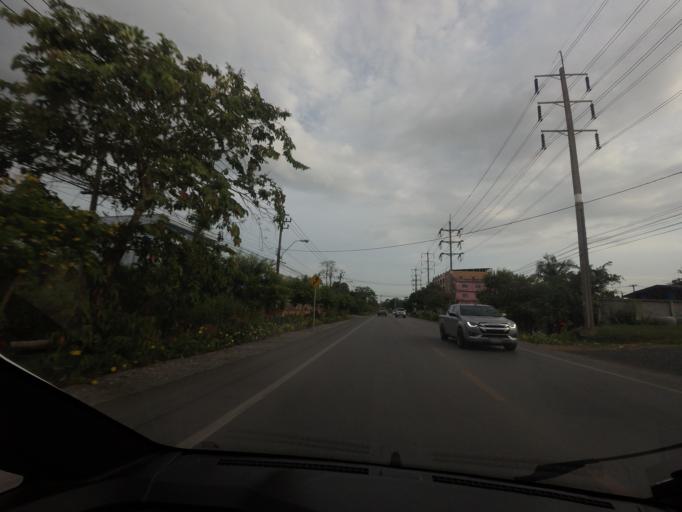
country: TH
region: Bangkok
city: Nong Chok
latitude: 13.8707
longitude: 100.8629
